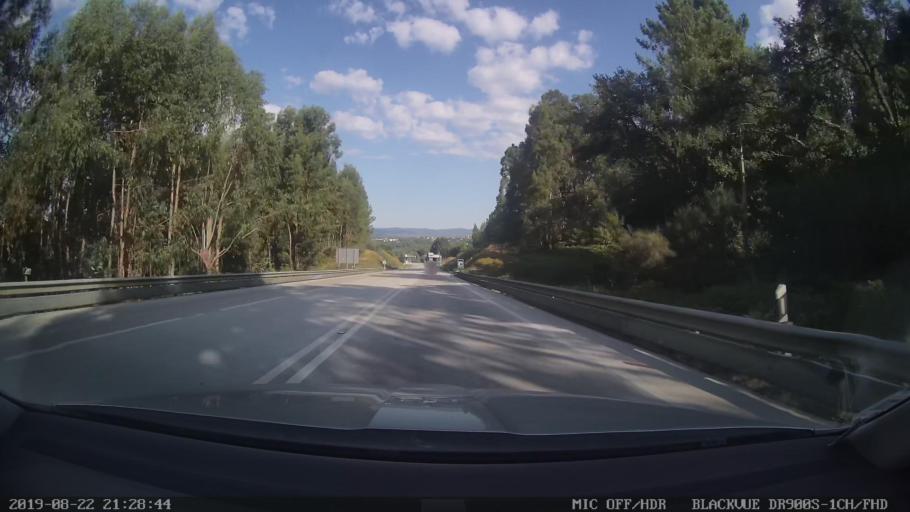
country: PT
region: Leiria
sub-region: Pedrogao Grande
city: Pedrogao Grande
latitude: 39.8962
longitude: -8.1241
